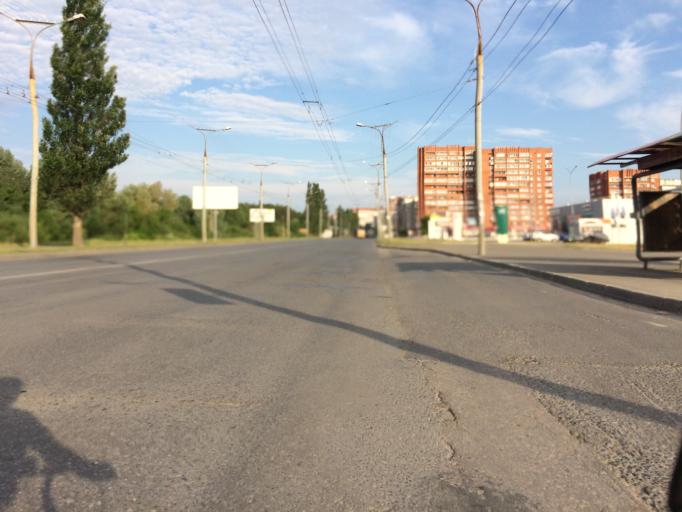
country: RU
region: Mariy-El
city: Yoshkar-Ola
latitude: 56.6245
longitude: 47.9295
